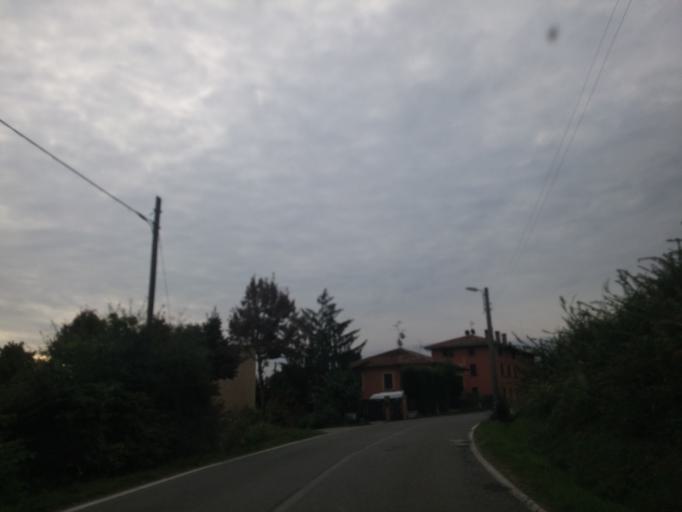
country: IT
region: Emilia-Romagna
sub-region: Provincia di Bologna
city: Longara
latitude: 44.5966
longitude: 11.3223
